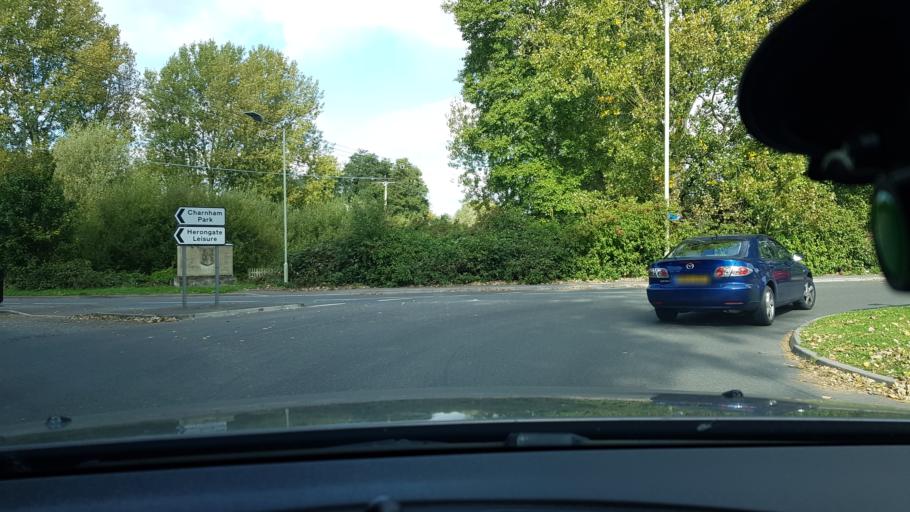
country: GB
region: England
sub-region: West Berkshire
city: Hungerford
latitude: 51.4189
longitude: -1.5108
